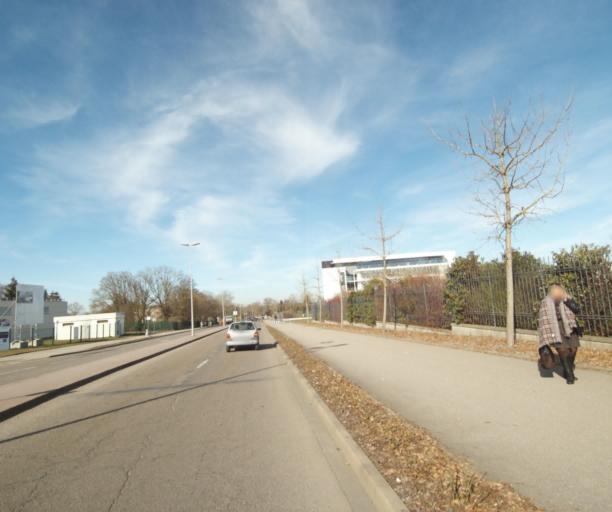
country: FR
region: Lorraine
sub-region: Departement de Meurthe-et-Moselle
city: Villers-les-Nancy
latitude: 48.6493
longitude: 6.1505
